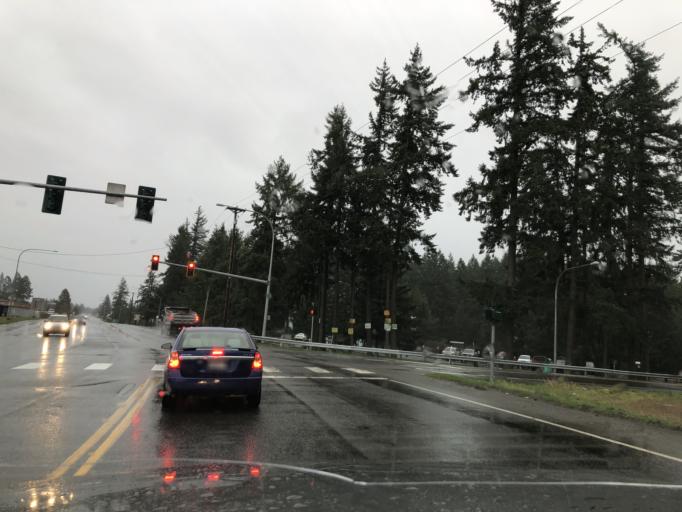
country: US
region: Washington
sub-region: Pierce County
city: Spanaway
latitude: 47.0836
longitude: -122.4350
